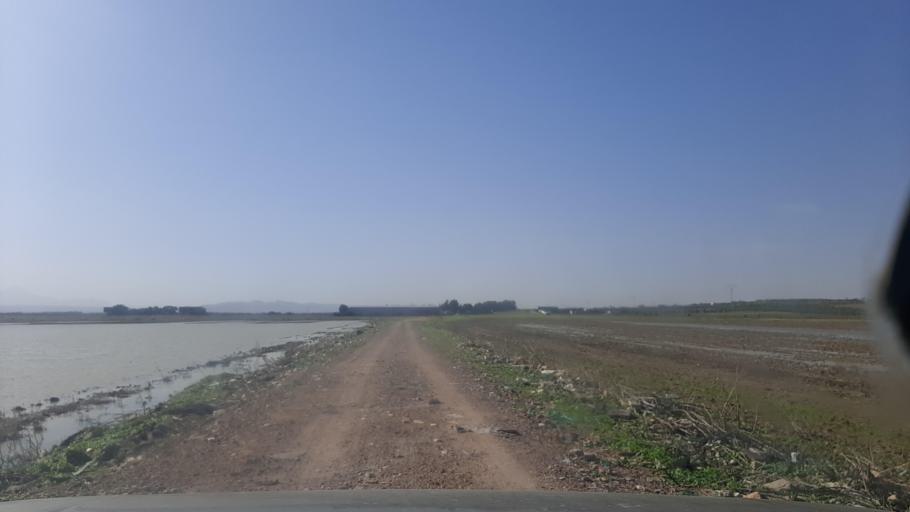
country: TN
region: Tunis
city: La Mohammedia
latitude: 36.6496
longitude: 10.0874
